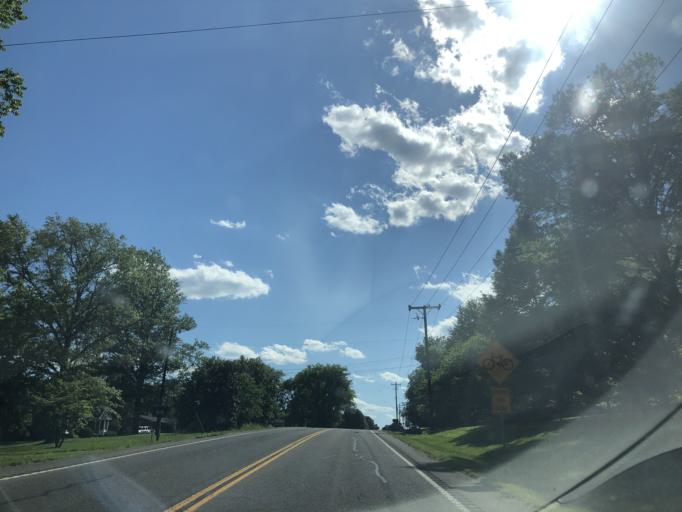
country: US
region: Tennessee
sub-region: Davidson County
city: Belle Meade
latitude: 36.0476
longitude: -86.9419
